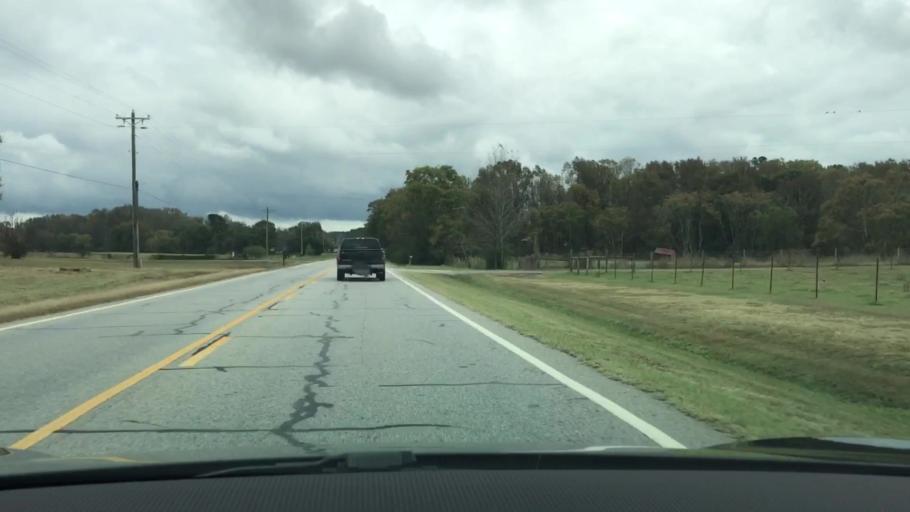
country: US
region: Georgia
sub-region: Oconee County
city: Watkinsville
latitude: 33.8244
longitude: -83.3707
